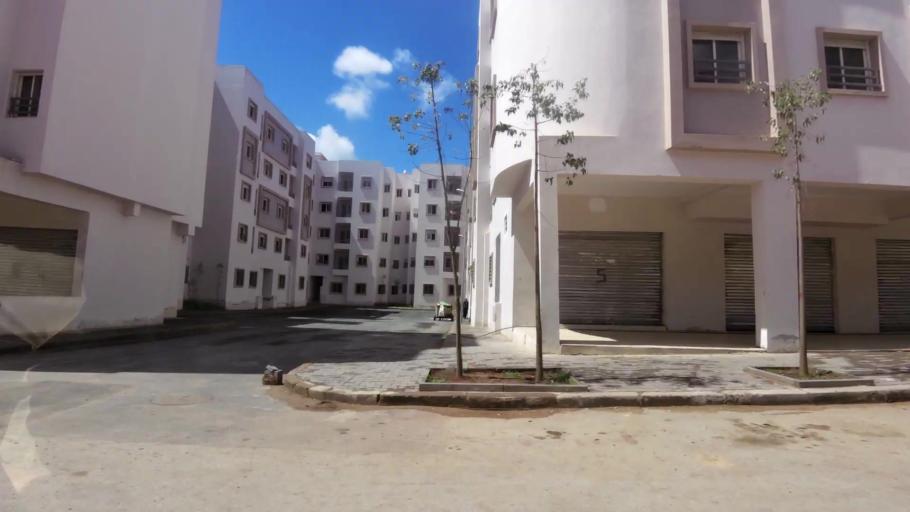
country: MA
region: Grand Casablanca
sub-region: Nouaceur
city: Dar Bouazza
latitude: 33.5352
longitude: -7.7324
